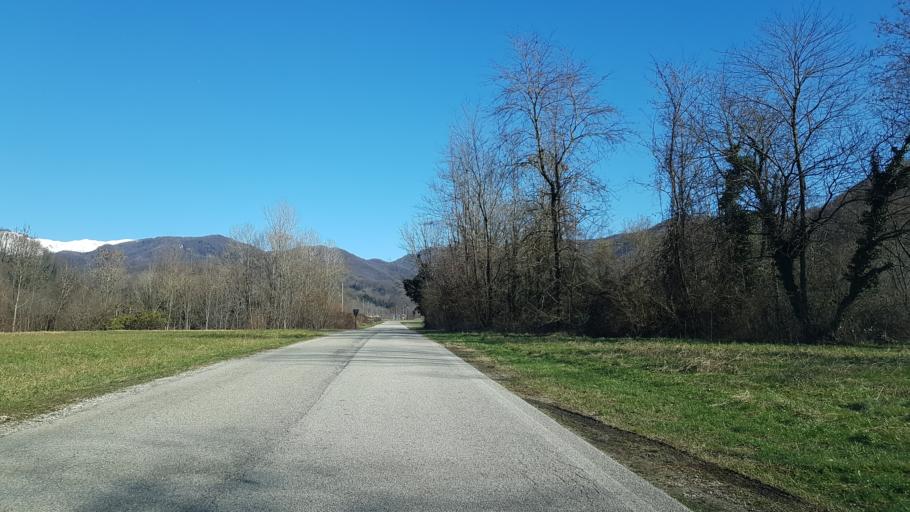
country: IT
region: Friuli Venezia Giulia
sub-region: Provincia di Udine
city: Nimis
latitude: 46.2016
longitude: 13.2848
